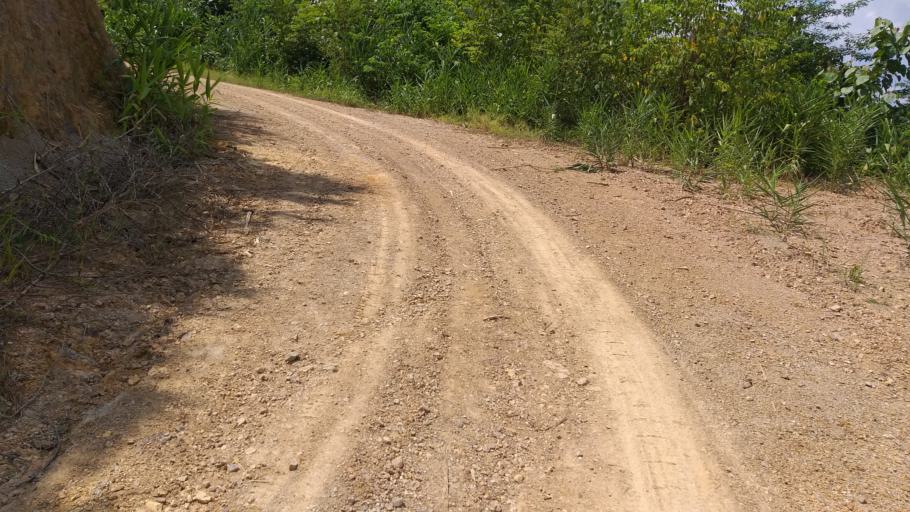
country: LA
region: Phongsali
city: Khoa
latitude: 21.3147
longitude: 102.5687
